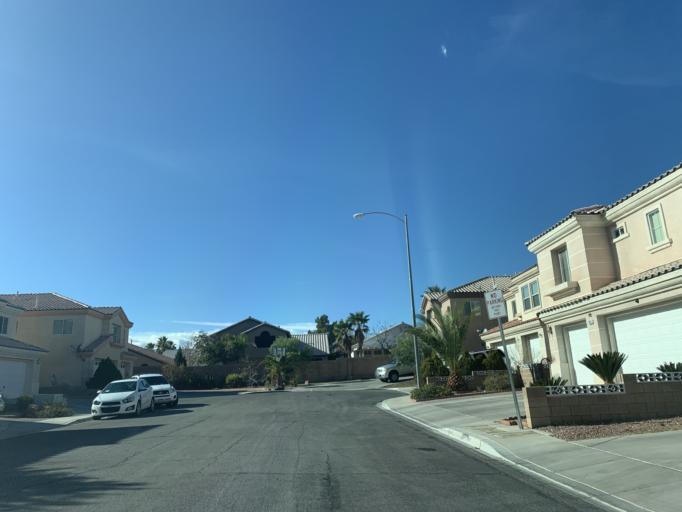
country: US
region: Nevada
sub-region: Clark County
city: Summerlin South
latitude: 36.1251
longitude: -115.3066
